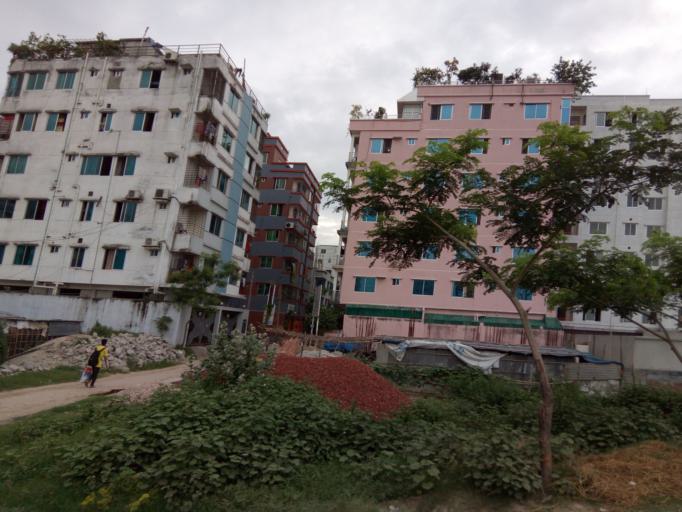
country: BD
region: Dhaka
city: Paltan
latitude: 23.7598
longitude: 90.4462
